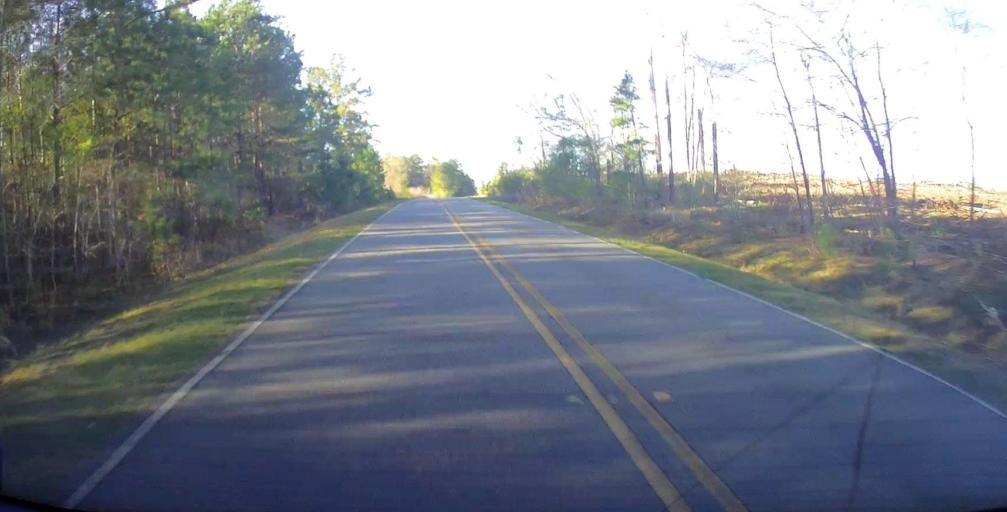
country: US
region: Georgia
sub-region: Pulaski County
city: Hawkinsville
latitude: 32.2877
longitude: -83.5910
